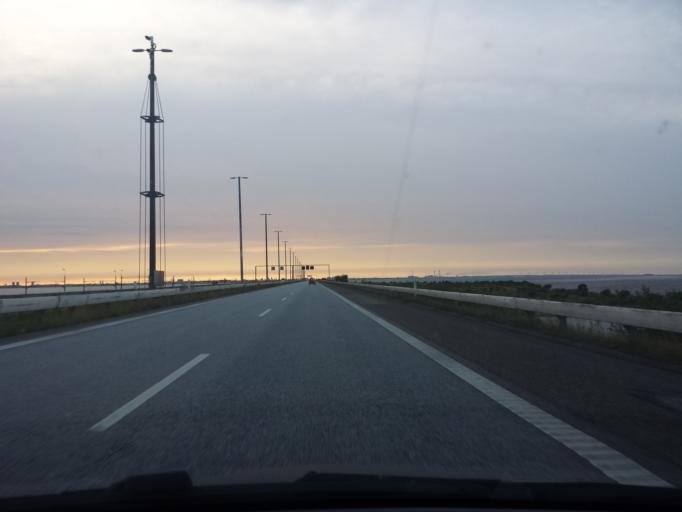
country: DK
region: Capital Region
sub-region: Dragor Kommune
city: Dragor
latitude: 55.6004
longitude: 12.7512
